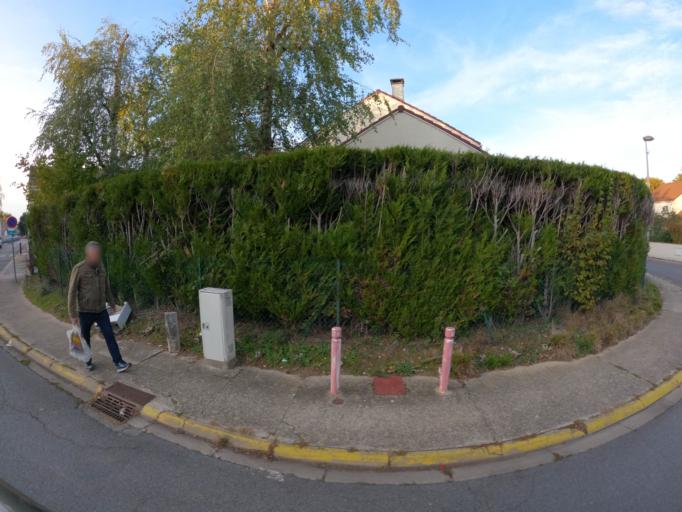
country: FR
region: Ile-de-France
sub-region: Departement de Seine-et-Marne
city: Emerainville
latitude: 48.8060
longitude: 2.6270
